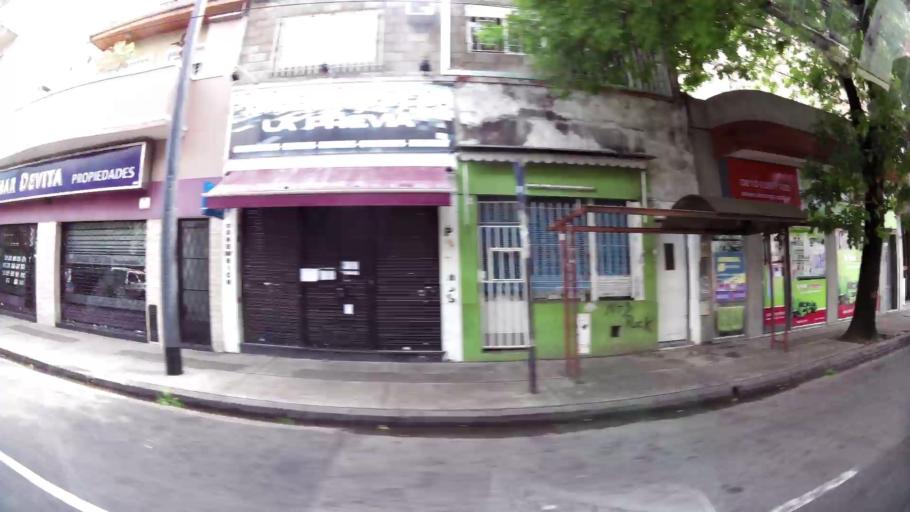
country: AR
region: Buenos Aires F.D.
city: Villa Santa Rita
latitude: -34.6170
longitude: -58.5213
